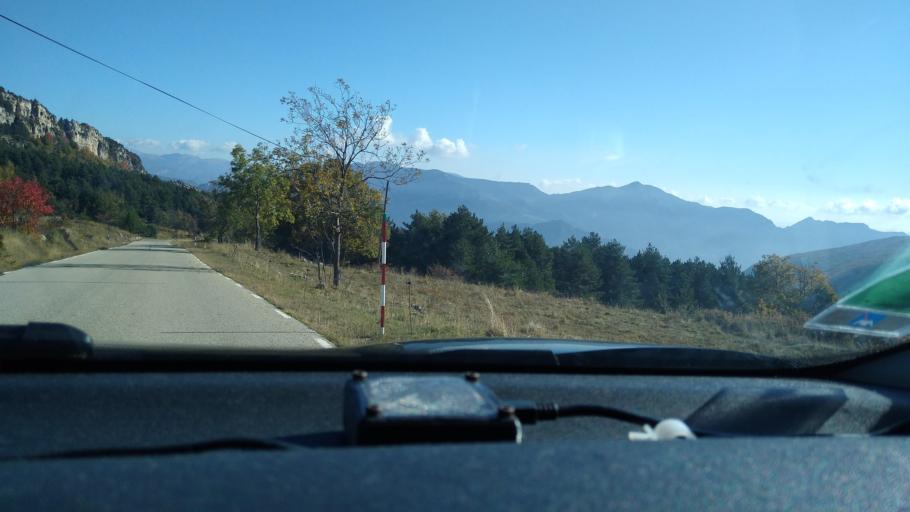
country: ES
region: Catalonia
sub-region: Provincia de Barcelona
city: Vallcebre
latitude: 42.1769
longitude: 1.8062
